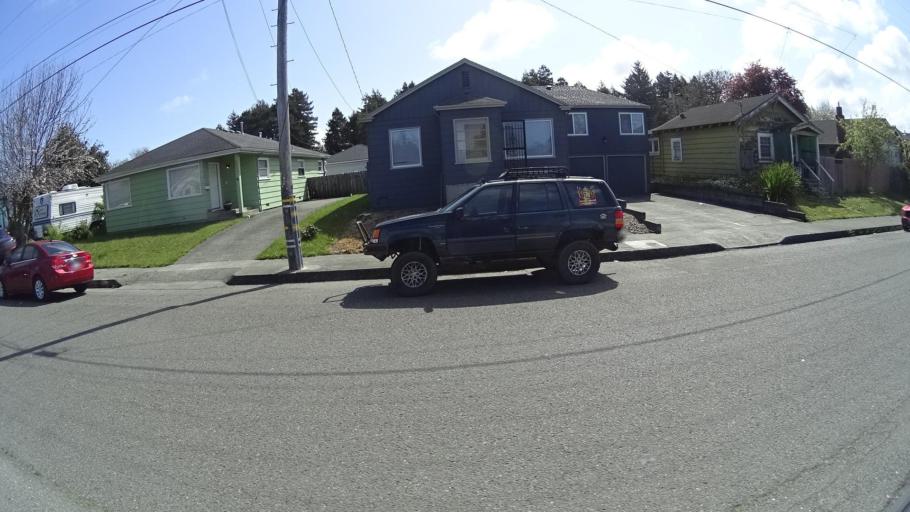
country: US
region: California
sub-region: Humboldt County
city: Cutten
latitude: 40.7775
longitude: -124.1613
